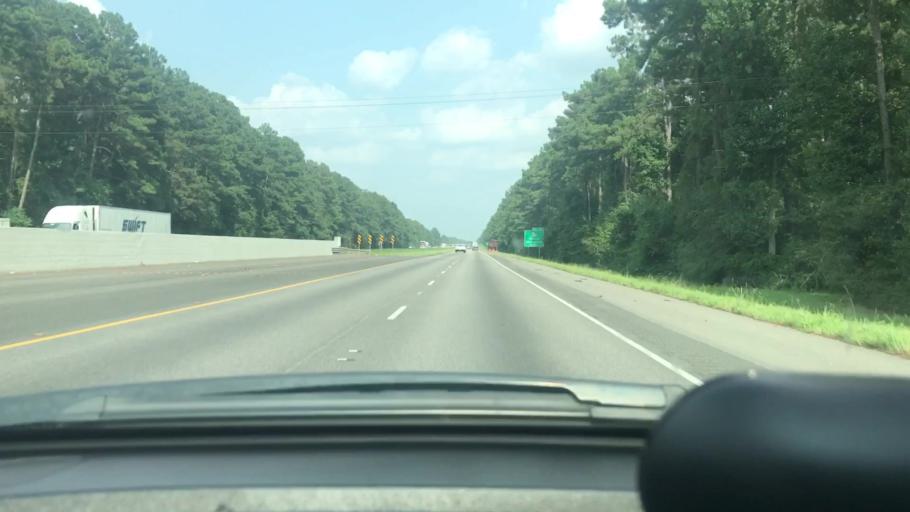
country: US
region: Louisiana
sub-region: Livingston Parish
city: Albany
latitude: 30.4766
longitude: -90.5926
